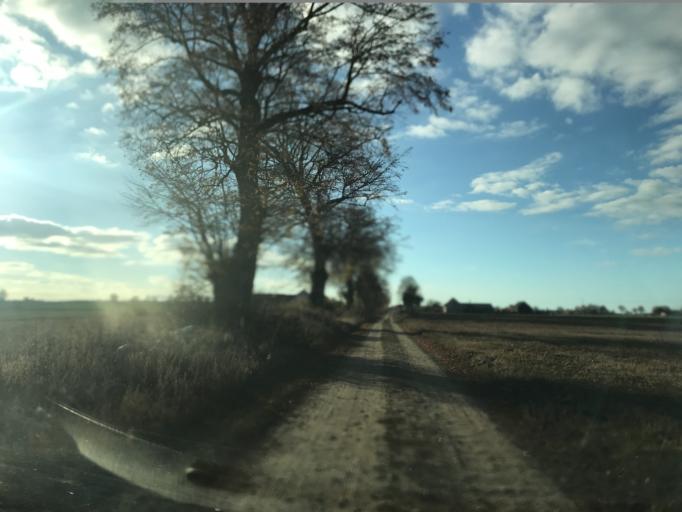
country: PL
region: Warmian-Masurian Voivodeship
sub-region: Powiat dzialdowski
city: Lidzbark
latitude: 53.3628
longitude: 19.8134
